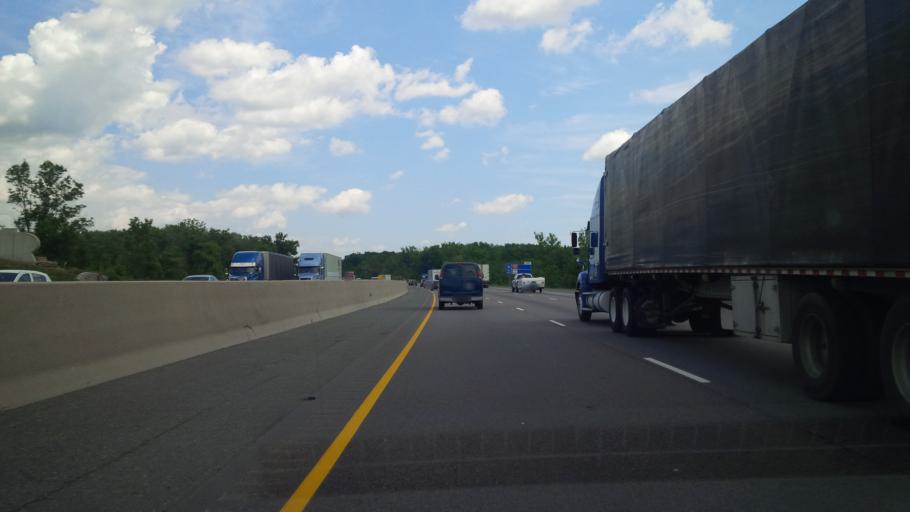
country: CA
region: Ontario
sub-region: Halton
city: Milton
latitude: 43.4727
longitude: -80.0412
